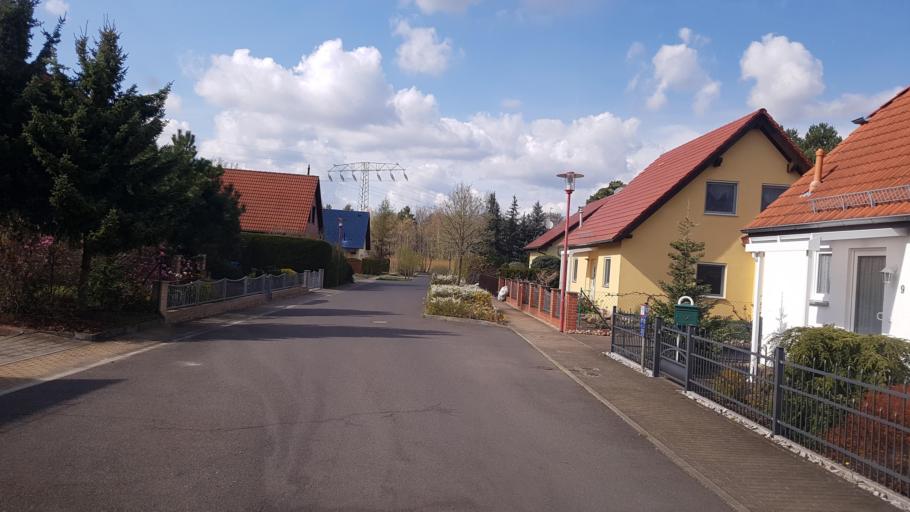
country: DE
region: Brandenburg
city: Luckenwalde
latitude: 52.0587
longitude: 13.1611
